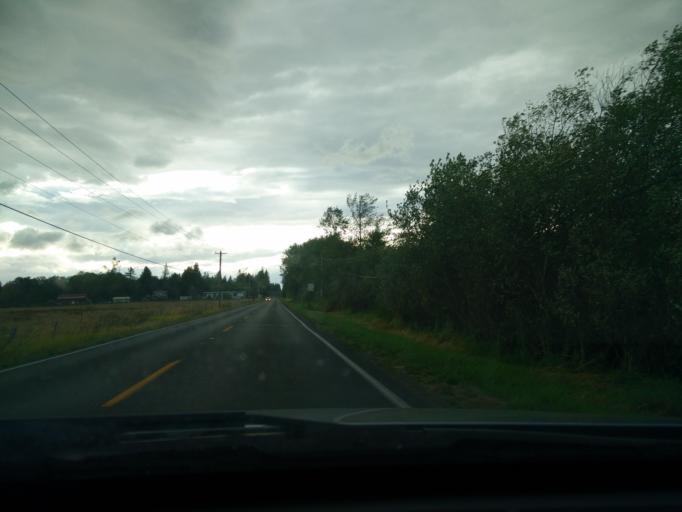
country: US
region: Washington
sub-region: Snohomish County
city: Stanwood
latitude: 48.2686
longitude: -122.3247
